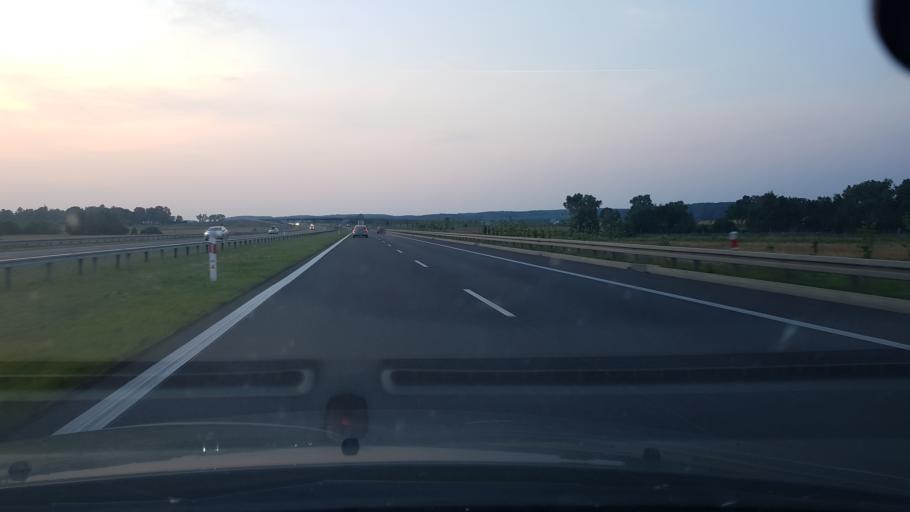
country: PL
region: Warmian-Masurian Voivodeship
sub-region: Powiat nidzicki
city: Nidzica
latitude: 53.3840
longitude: 20.3719
